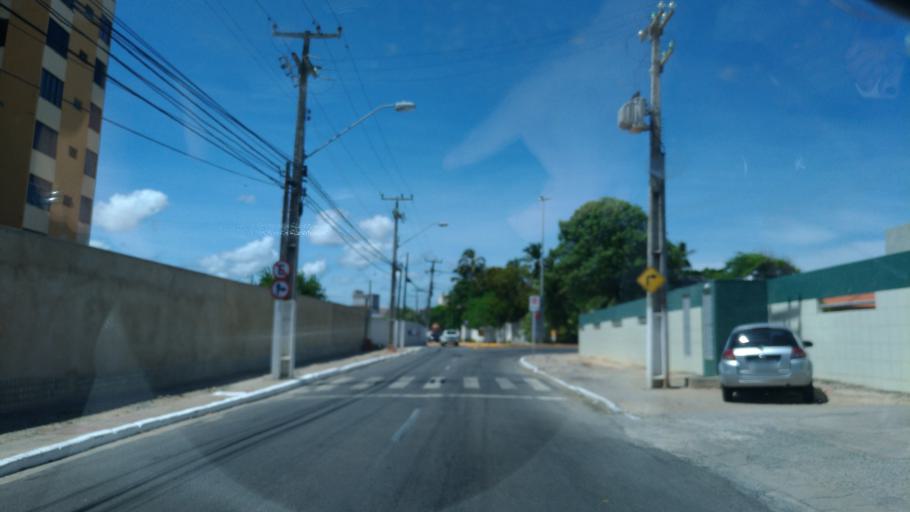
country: BR
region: Alagoas
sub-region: Maceio
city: Maceio
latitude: -9.6403
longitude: -35.7003
